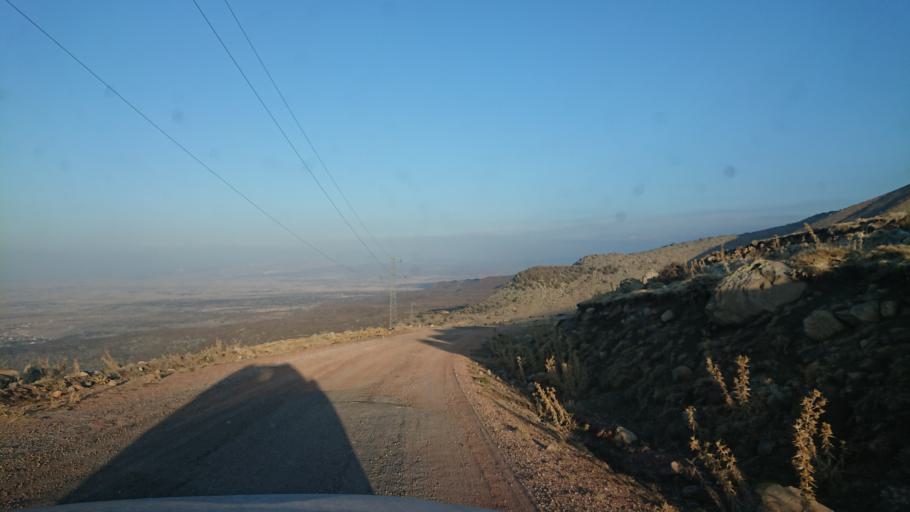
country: TR
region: Aksaray
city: Taspinar
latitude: 38.1612
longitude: 34.1729
